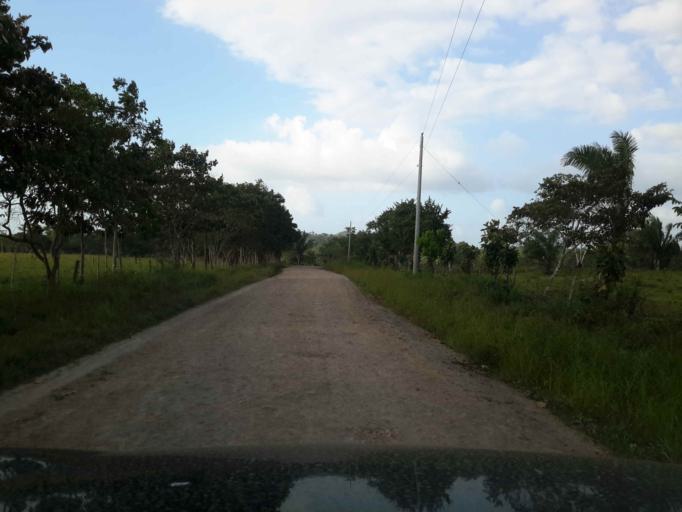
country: CR
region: Alajuela
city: Los Chiles
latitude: 11.1295
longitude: -84.6078
